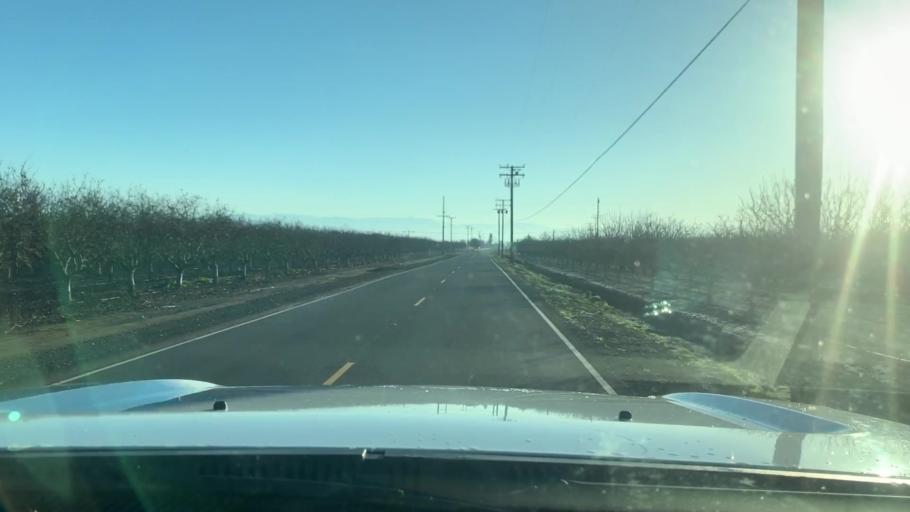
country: US
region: California
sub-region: Tulare County
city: Tulare
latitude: 36.2034
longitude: -119.4237
